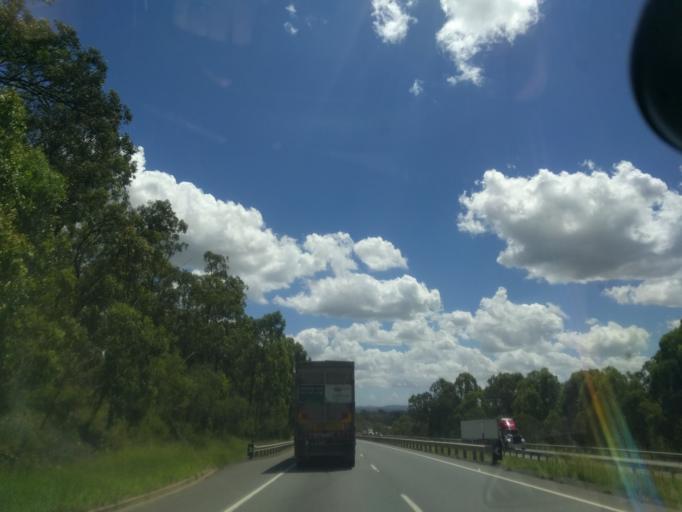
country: AU
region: Queensland
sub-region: Ipswich
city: Bundamba
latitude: -27.6118
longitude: 152.8274
